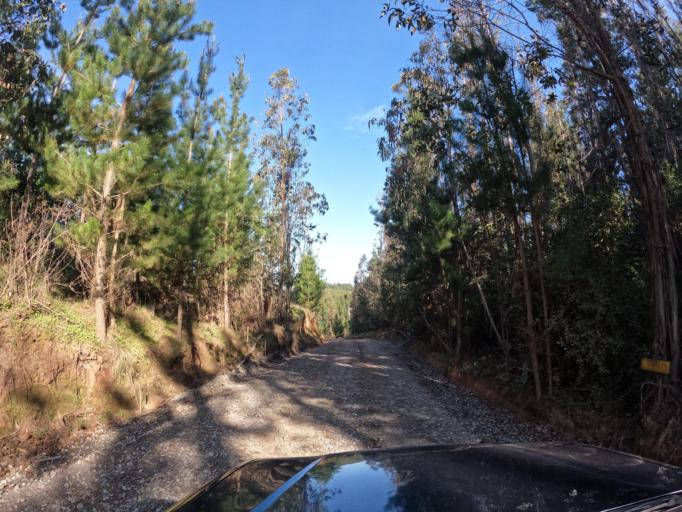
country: CL
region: Biobio
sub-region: Provincia de Biobio
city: La Laja
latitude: -37.0861
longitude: -72.7781
